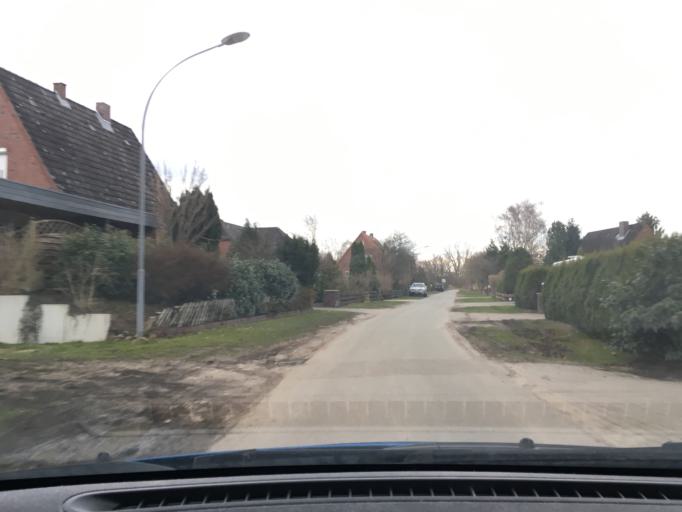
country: DE
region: Lower Saxony
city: Drage
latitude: 53.3709
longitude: 10.2680
